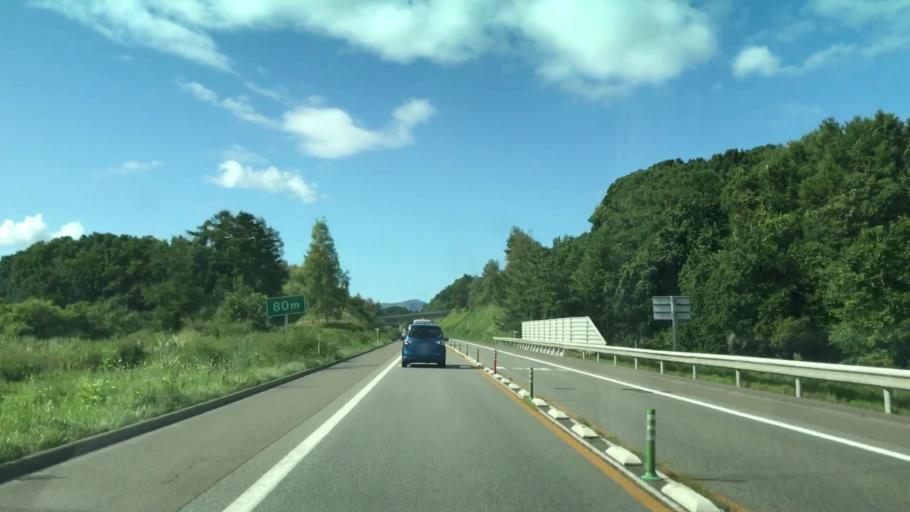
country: JP
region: Hokkaido
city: Date
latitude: 42.4358
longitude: 140.9217
